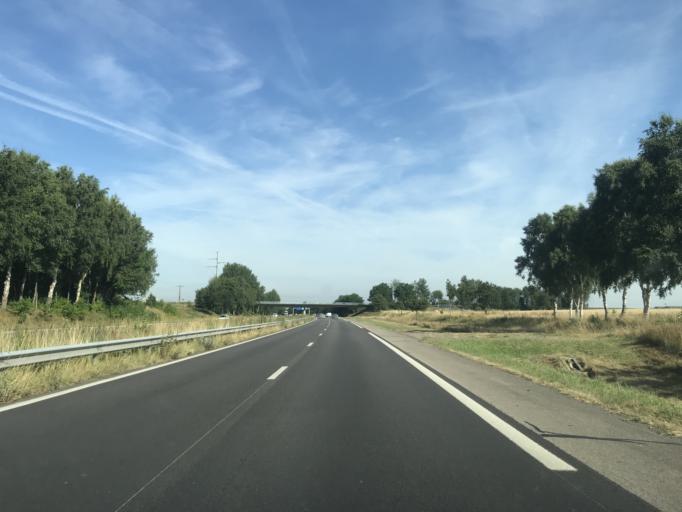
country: FR
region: Haute-Normandie
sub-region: Departement de la Seine-Maritime
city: Roumare
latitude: 49.5121
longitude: 0.9857
